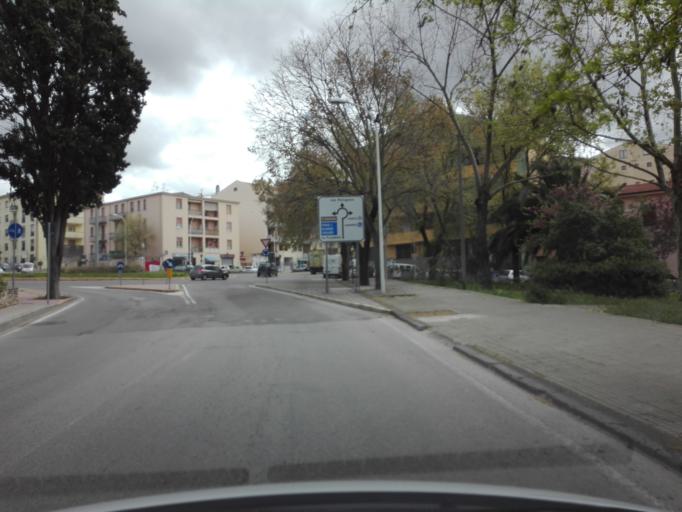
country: IT
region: Sardinia
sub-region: Provincia di Sassari
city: Sassari
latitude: 40.7377
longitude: 8.5600
